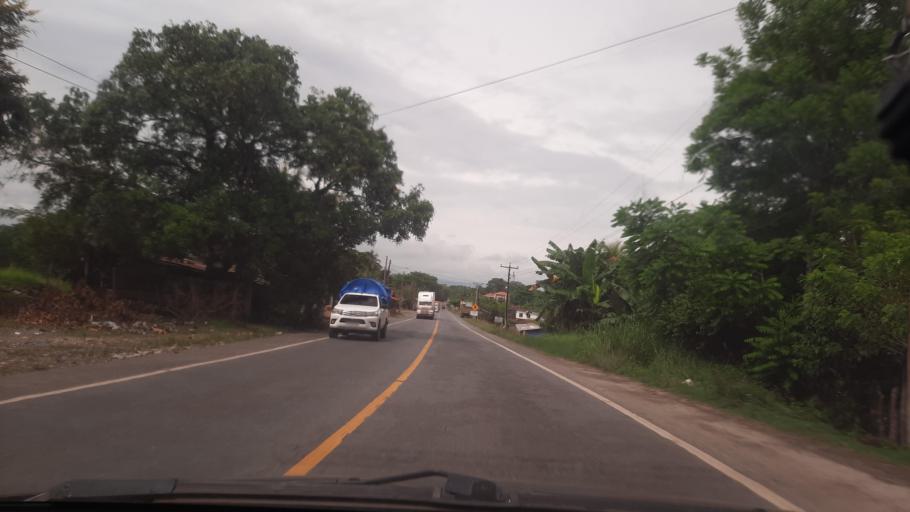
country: GT
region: Izabal
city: Morales
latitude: 15.5221
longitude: -88.7964
